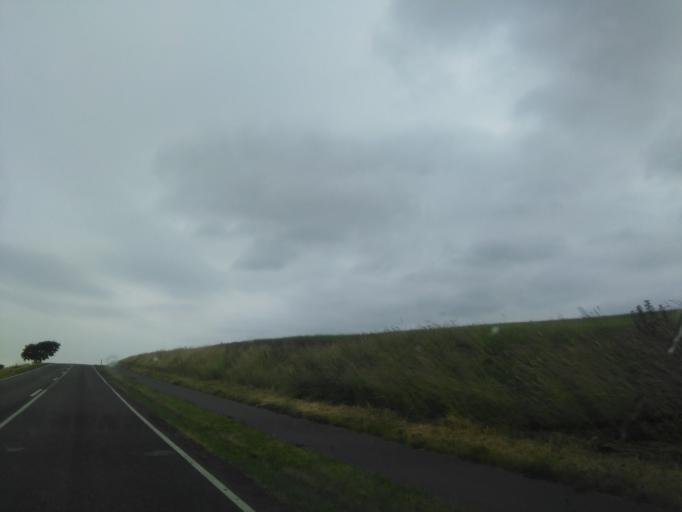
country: DK
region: Capital Region
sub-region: Bornholm Kommune
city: Akirkeby
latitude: 55.0477
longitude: 14.8284
